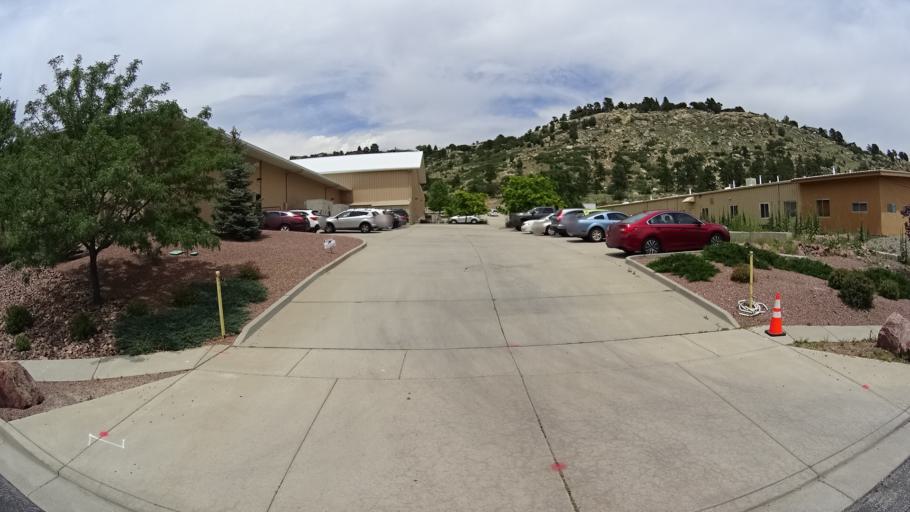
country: US
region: Colorado
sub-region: El Paso County
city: Colorado Springs
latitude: 38.9006
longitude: -104.8400
